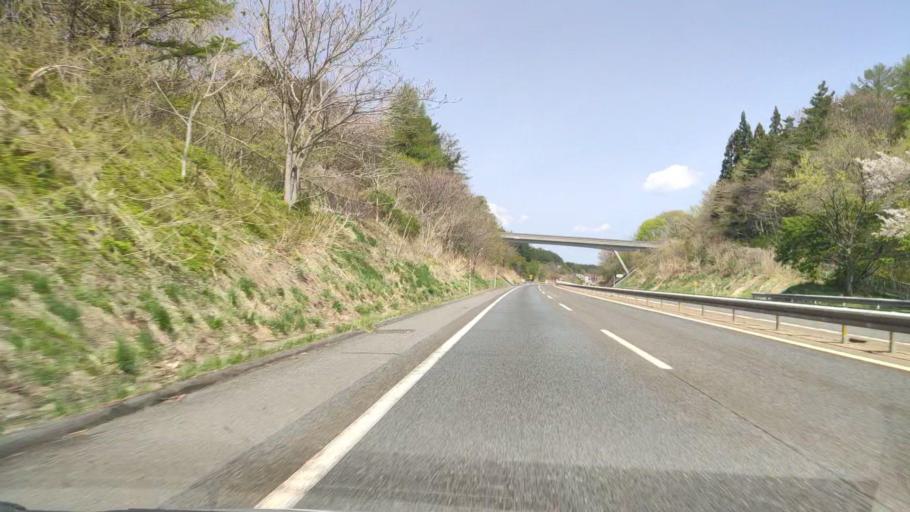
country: JP
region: Iwate
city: Ichinohe
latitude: 40.2608
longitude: 141.4009
